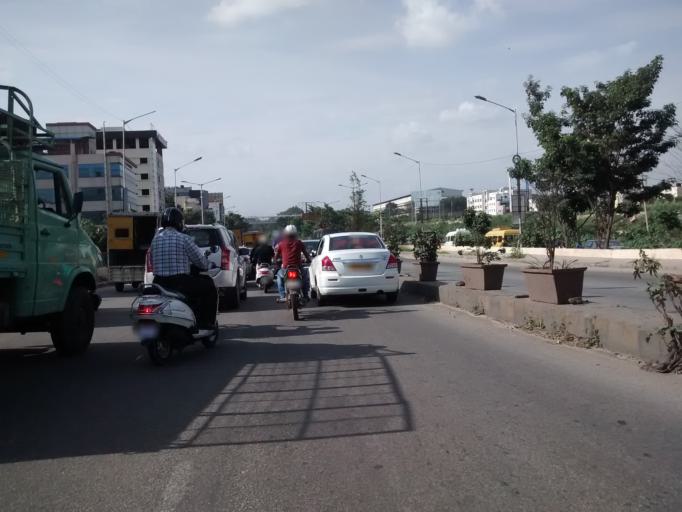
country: IN
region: Karnataka
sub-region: Bangalore Urban
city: Bangalore
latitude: 13.0007
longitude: 77.6634
